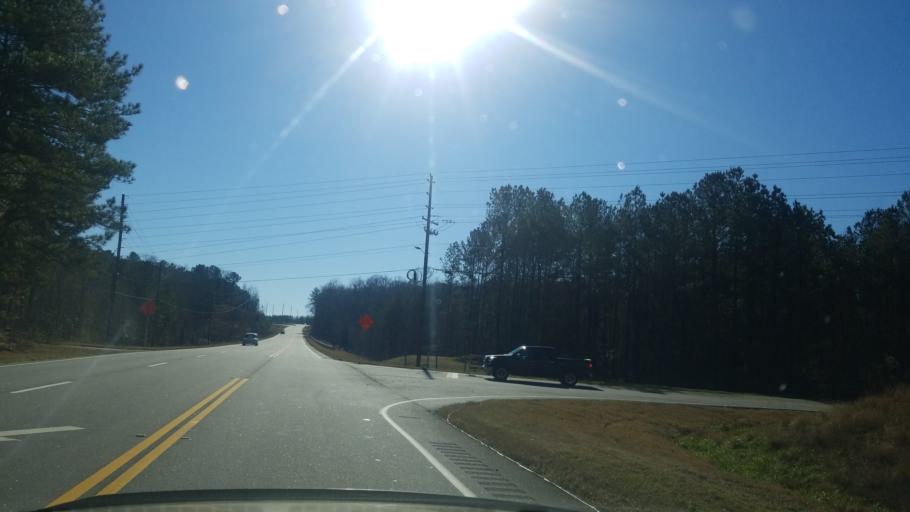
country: US
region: Georgia
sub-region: Troup County
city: West Point
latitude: 32.8616
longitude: -85.1358
